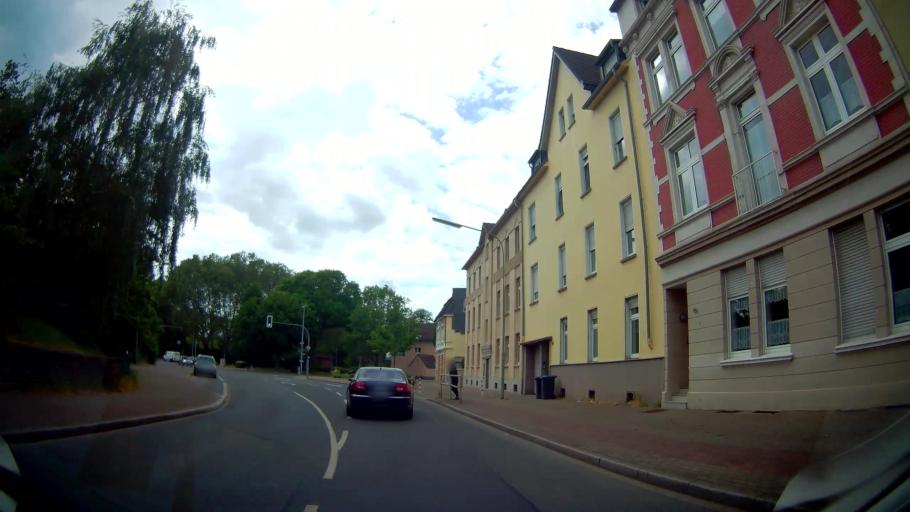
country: DE
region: North Rhine-Westphalia
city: Bochum-Hordel
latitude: 51.5229
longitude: 7.1610
